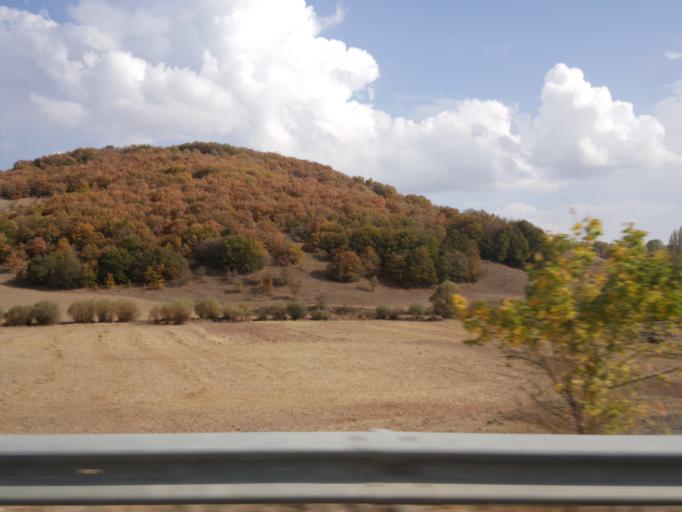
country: TR
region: Corum
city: Alaca
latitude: 40.3058
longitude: 34.6556
